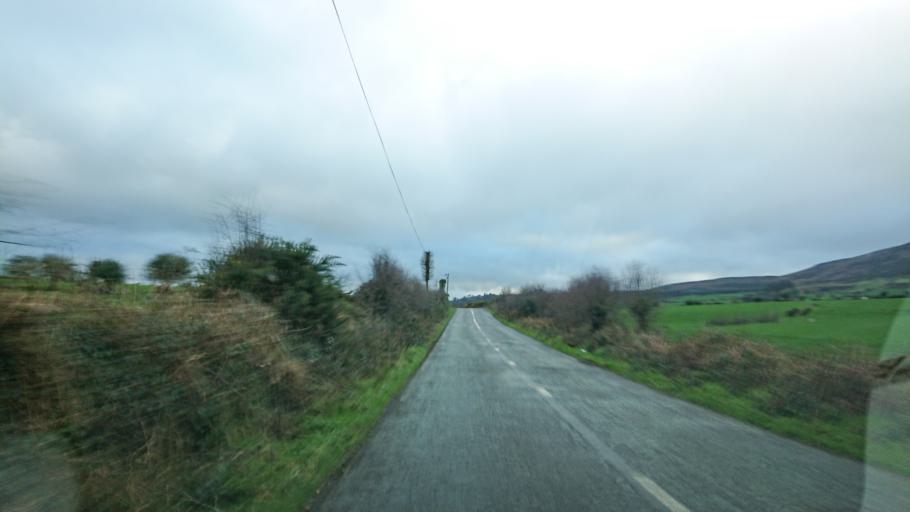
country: IE
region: Munster
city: Carrick-on-Suir
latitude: 52.2506
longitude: -7.4121
